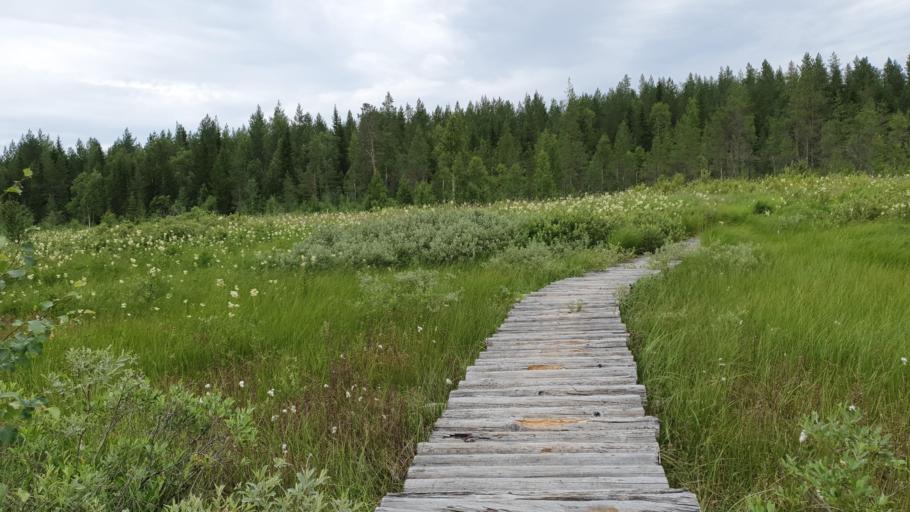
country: RU
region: Republic of Karelia
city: Kostomuksha
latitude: 64.7577
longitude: 30.0006
